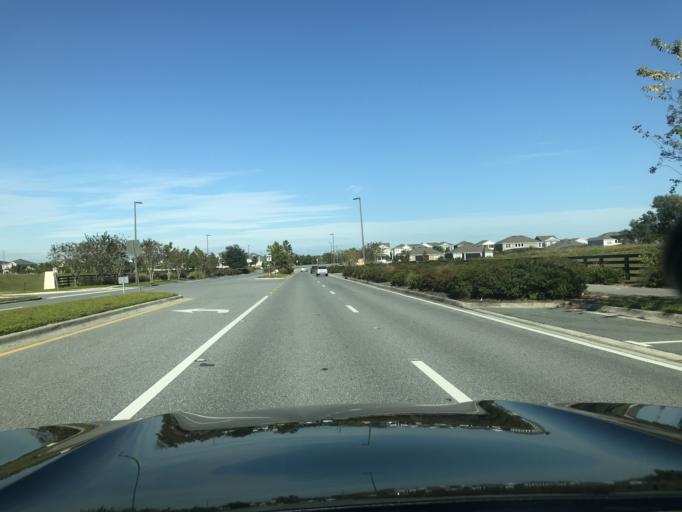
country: US
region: Florida
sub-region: Orange County
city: Lake Butler
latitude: 28.4618
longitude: -81.6252
